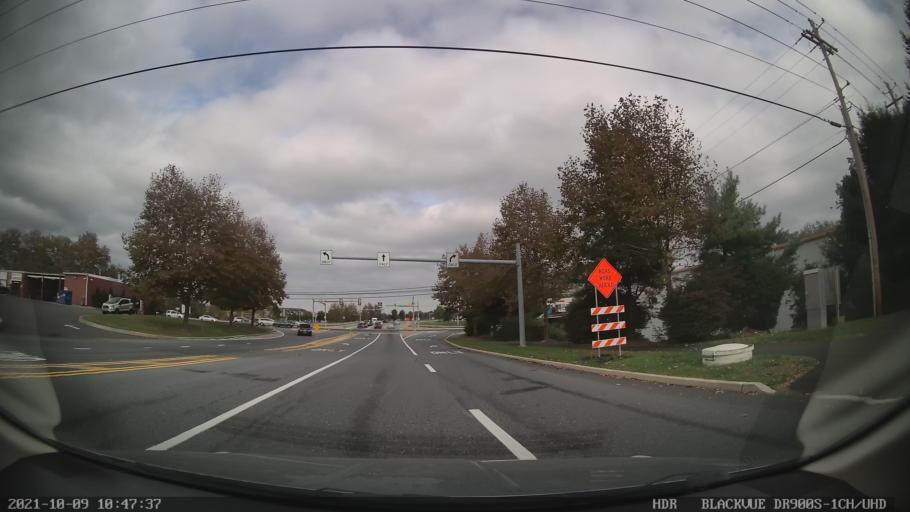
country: US
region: Pennsylvania
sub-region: Lehigh County
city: Ancient Oaks
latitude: 40.5544
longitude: -75.5819
